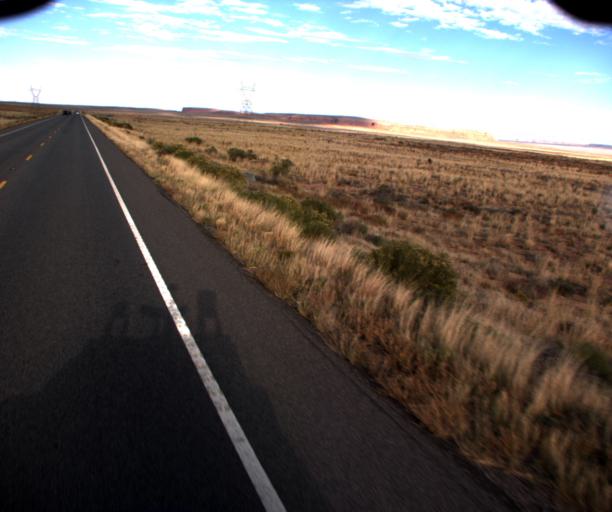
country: US
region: Arizona
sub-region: Apache County
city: Lukachukai
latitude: 36.9345
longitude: -109.2320
